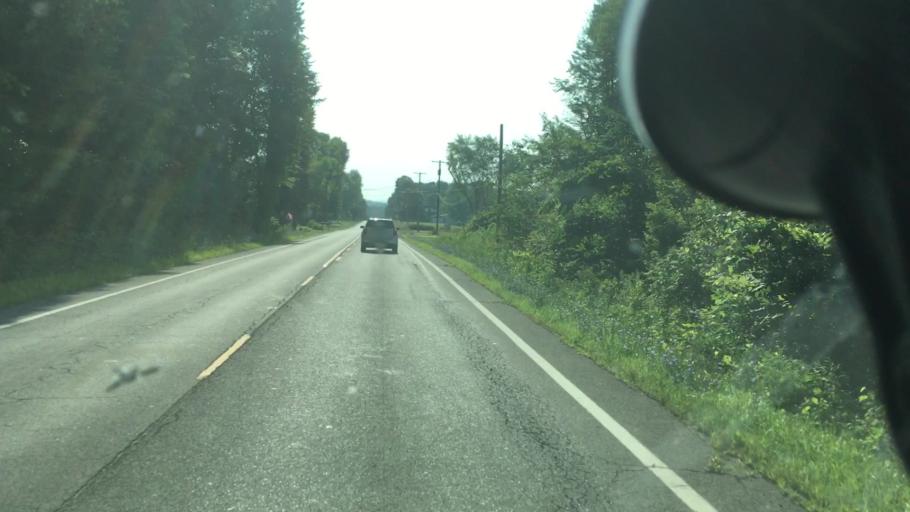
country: US
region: Ohio
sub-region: Mahoning County
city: Lowellville
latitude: 41.0239
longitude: -80.5386
